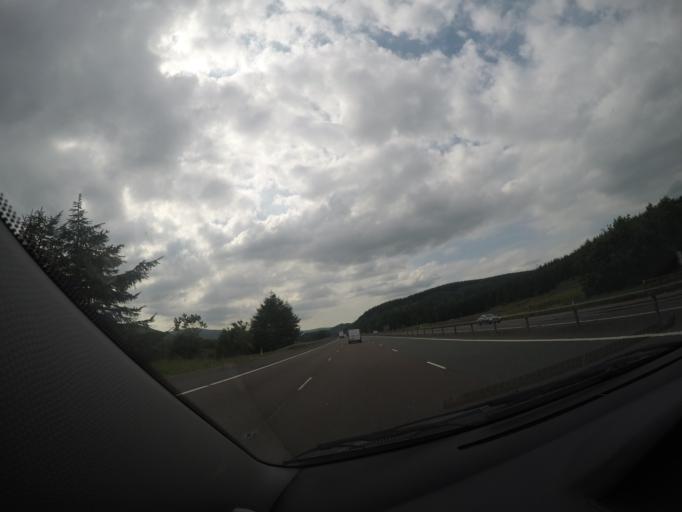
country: GB
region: Scotland
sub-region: Dumfries and Galloway
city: Moffat
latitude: 55.4256
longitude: -3.5995
